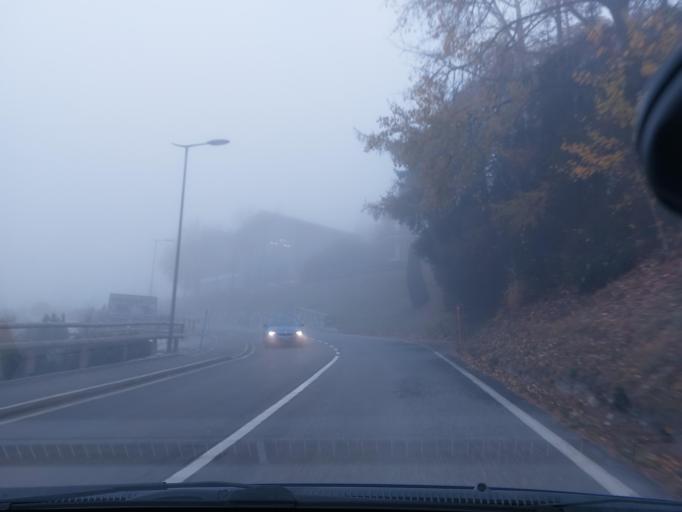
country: CH
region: Valais
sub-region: Sierre District
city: Lens
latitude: 46.2936
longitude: 7.4506
